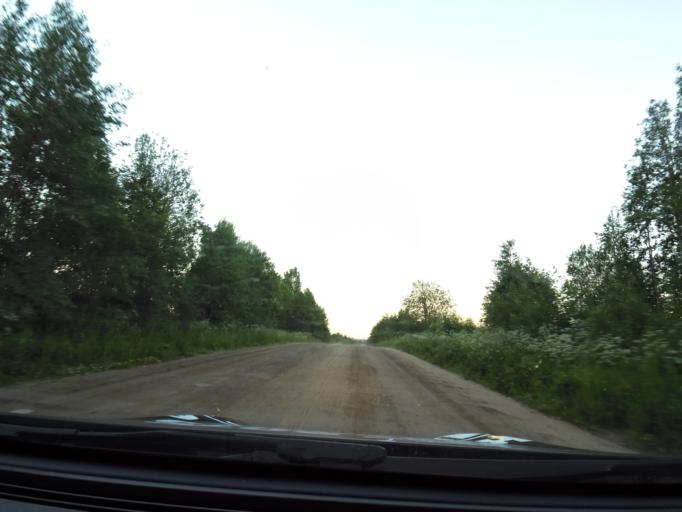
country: RU
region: Leningrad
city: Voznesen'ye
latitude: 60.8809
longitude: 35.5217
